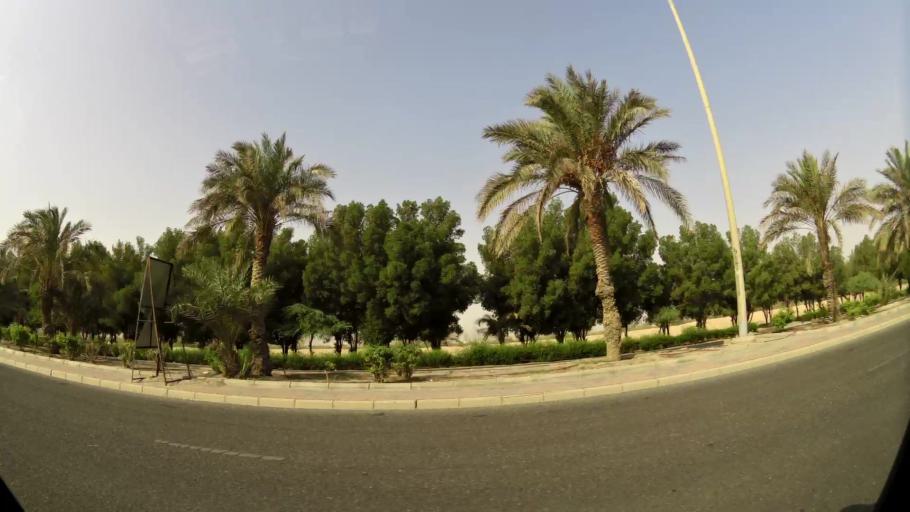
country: KW
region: Al Asimah
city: Ar Rabiyah
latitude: 29.3309
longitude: 47.7994
